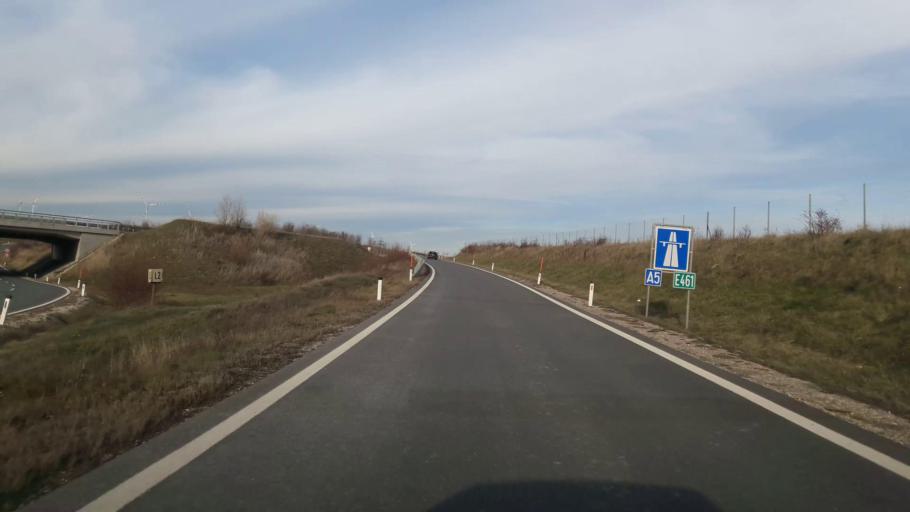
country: AT
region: Lower Austria
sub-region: Politischer Bezirk Mistelbach
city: Gaweinstal
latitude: 48.4932
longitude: 16.5976
